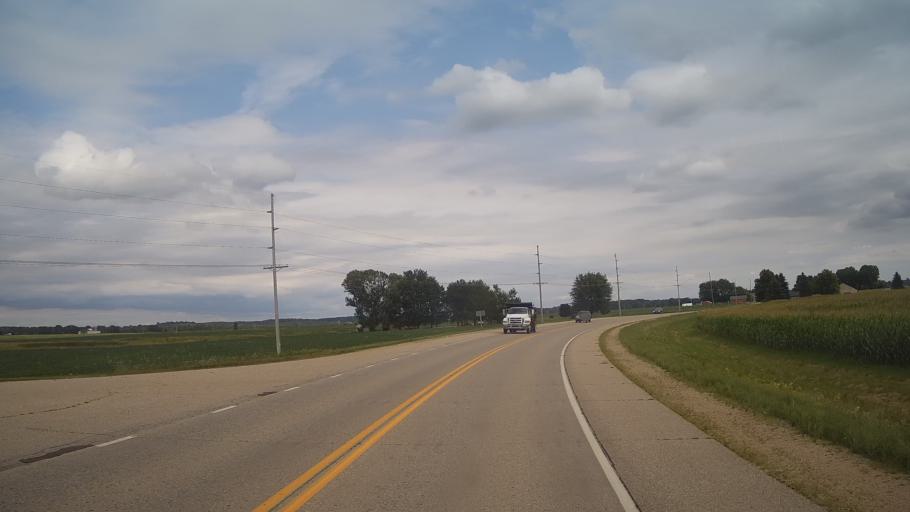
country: US
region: Wisconsin
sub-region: Waushara County
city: Redgranite
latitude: 44.0410
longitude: -89.0416
